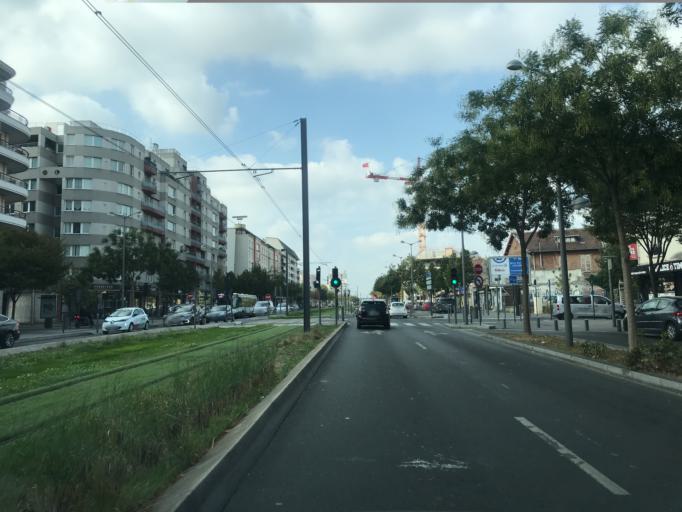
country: FR
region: Ile-de-France
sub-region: Departement des Hauts-de-Seine
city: La Garenne-Colombes
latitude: 48.9115
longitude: 2.2331
